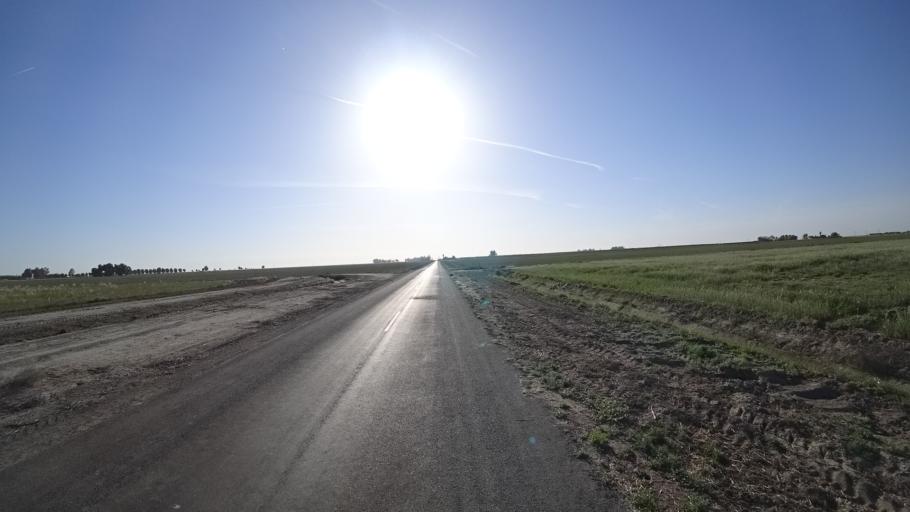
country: US
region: California
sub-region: Kings County
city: Stratford
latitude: 36.1674
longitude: -119.7900
